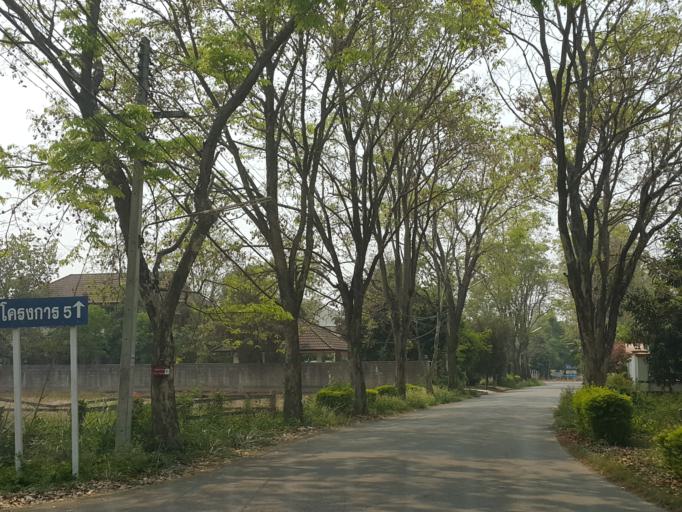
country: TH
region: Chiang Mai
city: Chiang Mai
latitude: 18.7315
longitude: 98.9713
